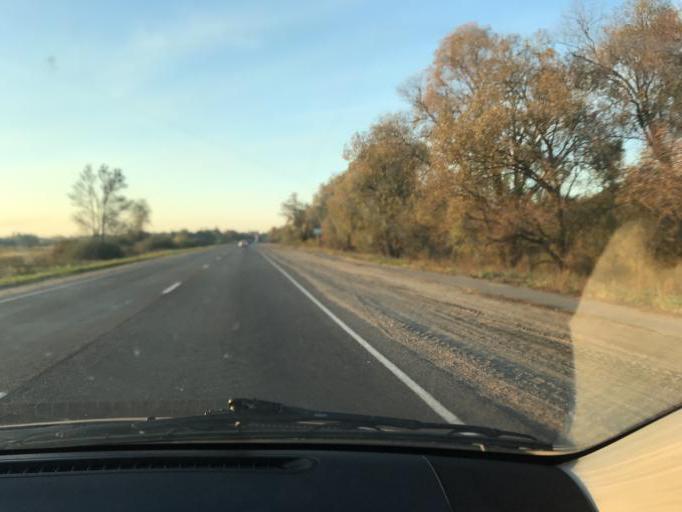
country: BY
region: Brest
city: Pinsk
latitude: 52.0979
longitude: 26.1183
